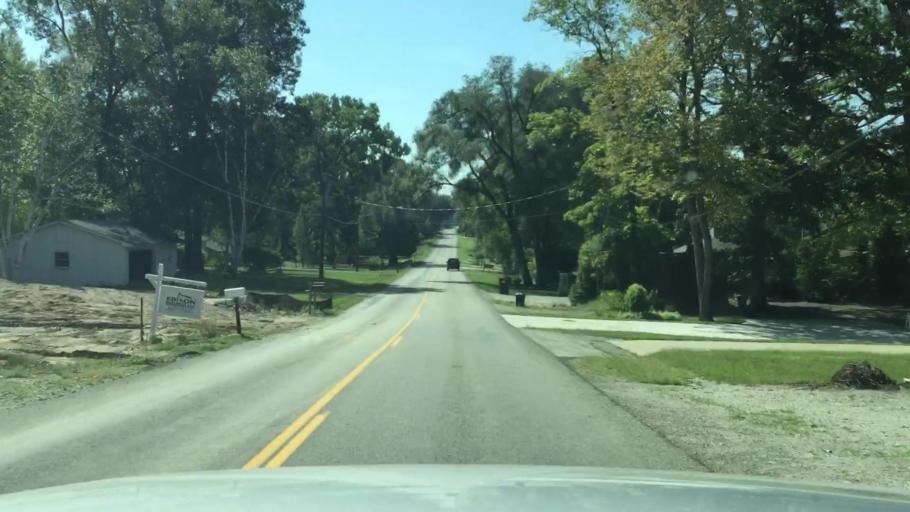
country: US
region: Michigan
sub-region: Lenawee County
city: Manitou Beach-Devils Lake
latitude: 41.9957
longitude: -84.2808
